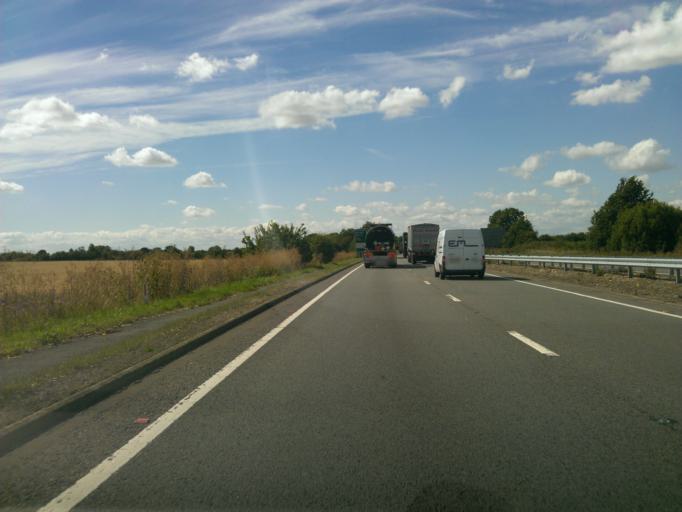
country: GB
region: England
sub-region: Cambridgeshire
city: Buckden
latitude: 52.3373
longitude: -0.3264
